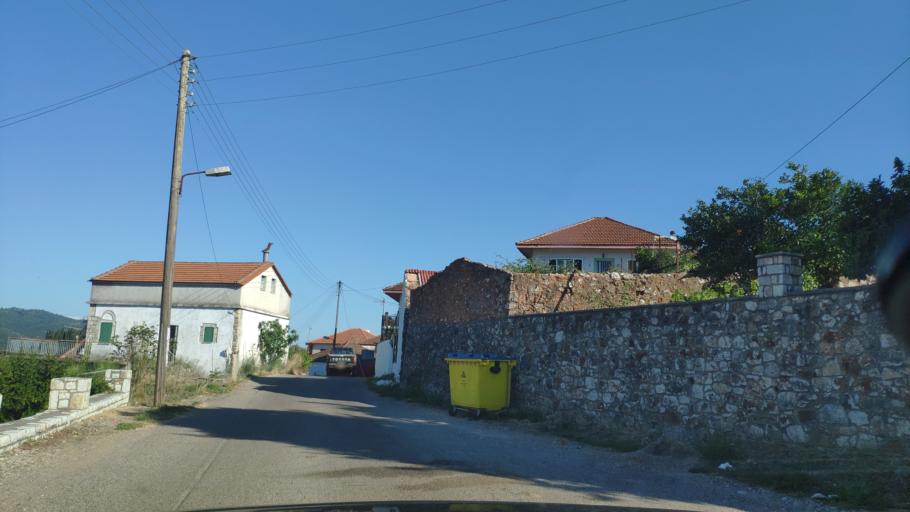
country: GR
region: West Greece
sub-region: Nomos Aitolias kai Akarnanias
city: Fitiai
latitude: 38.6626
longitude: 21.1450
